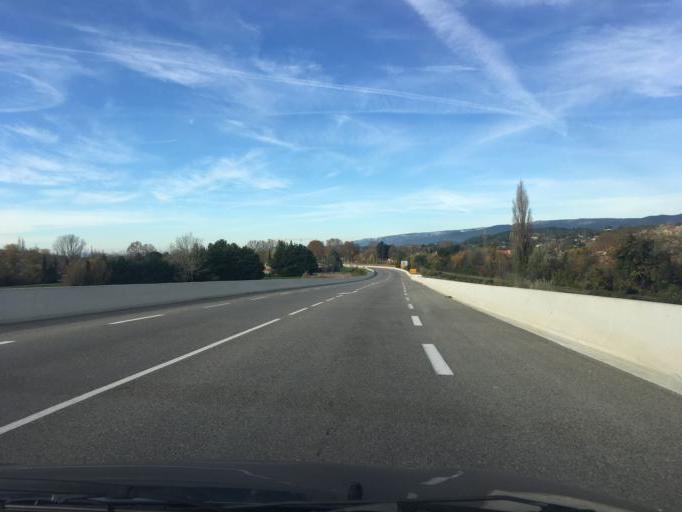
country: FR
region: Provence-Alpes-Cote d'Azur
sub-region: Departement du Vaucluse
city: Cadenet
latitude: 43.7268
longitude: 5.3794
